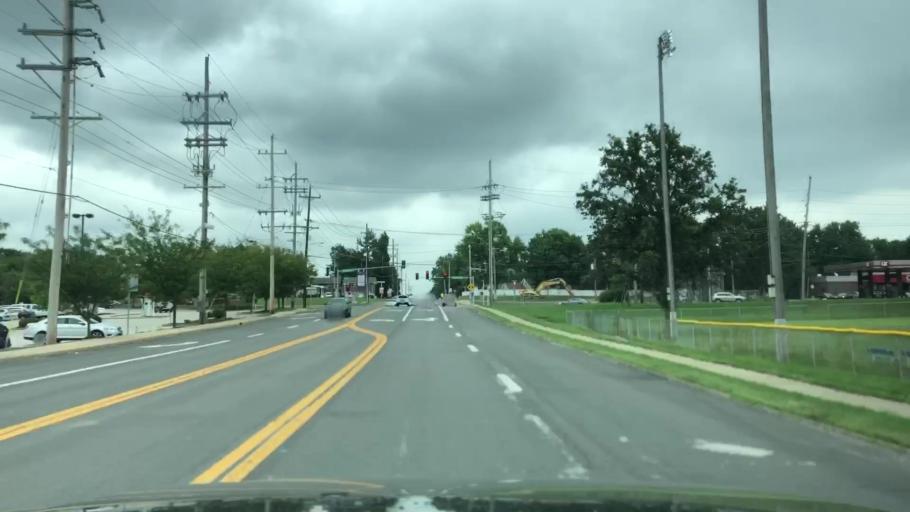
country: US
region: Missouri
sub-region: Saint Louis County
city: Hazelwood
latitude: 38.8095
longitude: -90.3599
